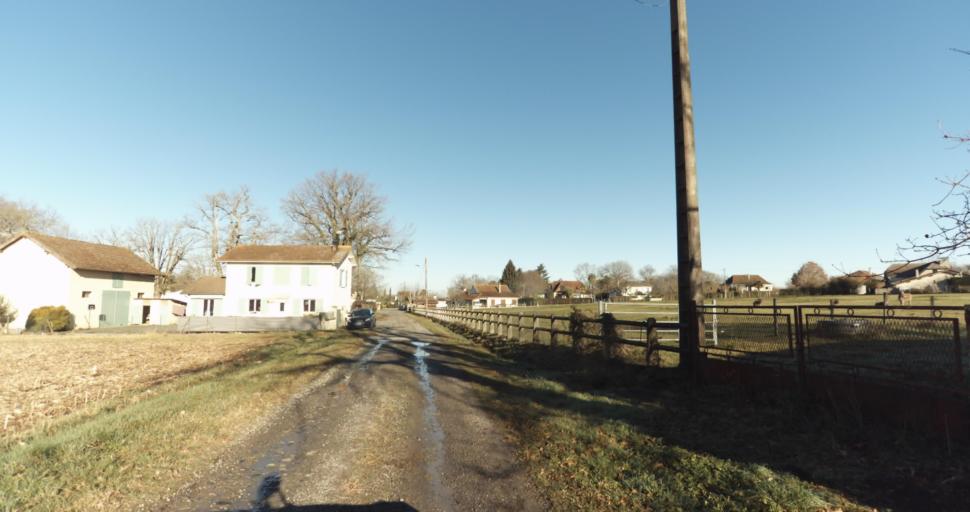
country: FR
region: Aquitaine
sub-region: Departement des Pyrenees-Atlantiques
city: Morlaas
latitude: 43.3340
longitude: -0.2465
